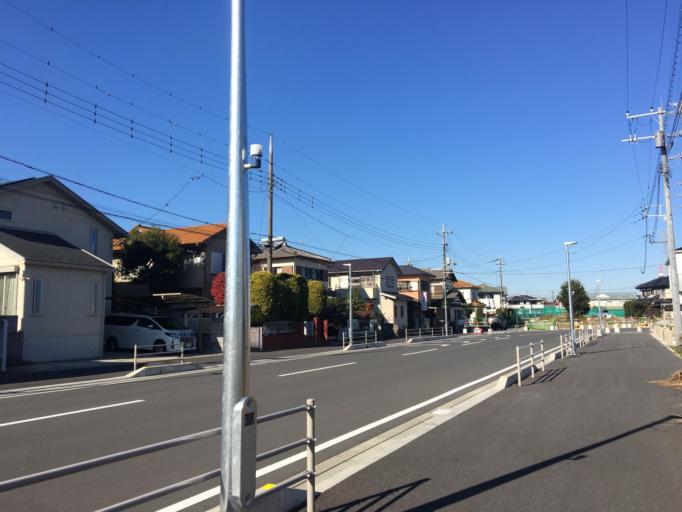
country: JP
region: Saitama
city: Satte
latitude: 36.0725
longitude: 139.7097
